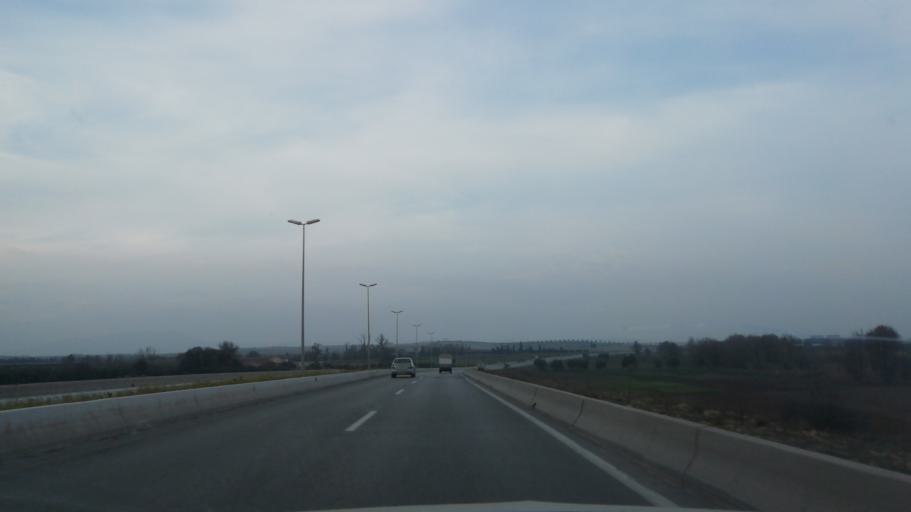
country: DZ
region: Sidi Bel Abbes
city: Sidi Bel Abbes
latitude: 35.1875
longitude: -0.6604
